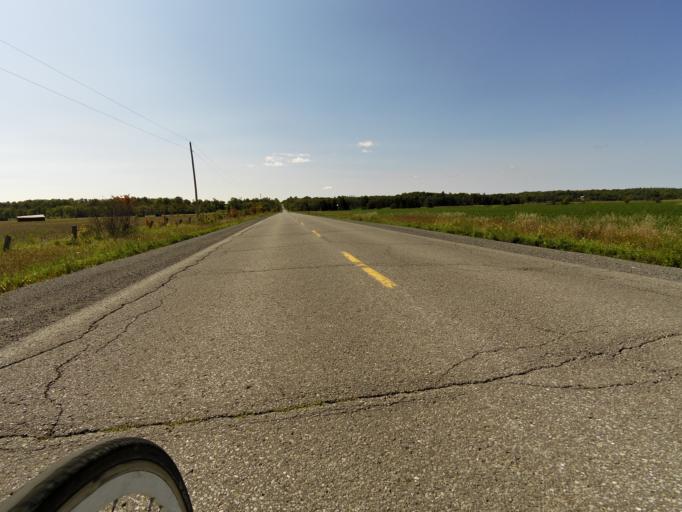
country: CA
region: Ontario
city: Bells Corners
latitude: 45.4117
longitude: -76.0374
